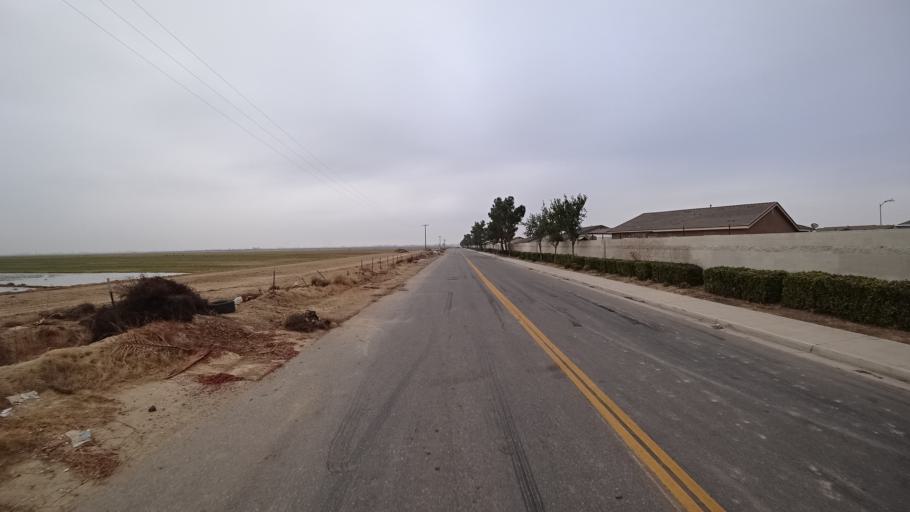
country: US
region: California
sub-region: Kern County
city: Lamont
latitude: 35.3397
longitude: -118.9411
